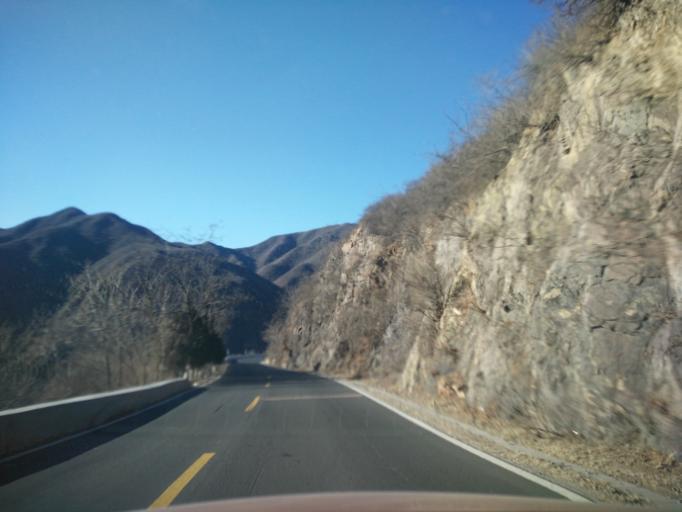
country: CN
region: Beijing
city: Wangping
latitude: 40.0031
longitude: 115.9475
